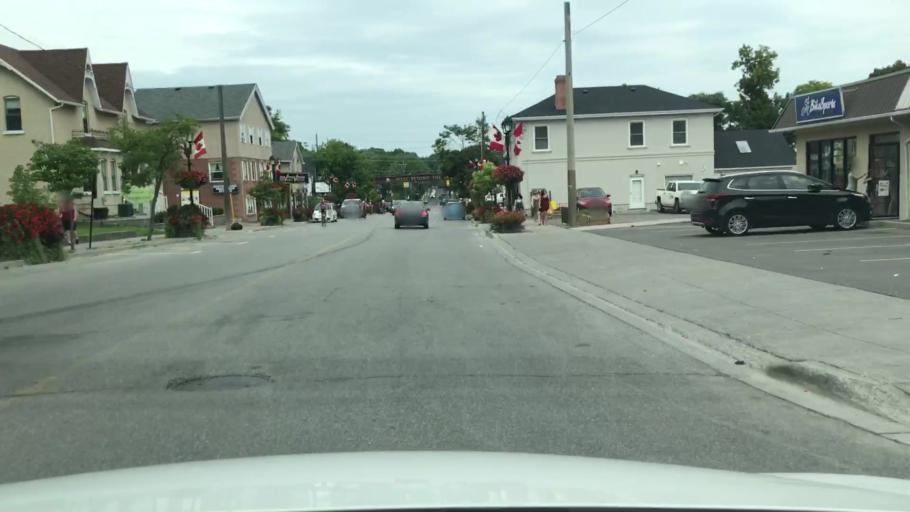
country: CA
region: Ontario
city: Newmarket
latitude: 44.0574
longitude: -79.4604
